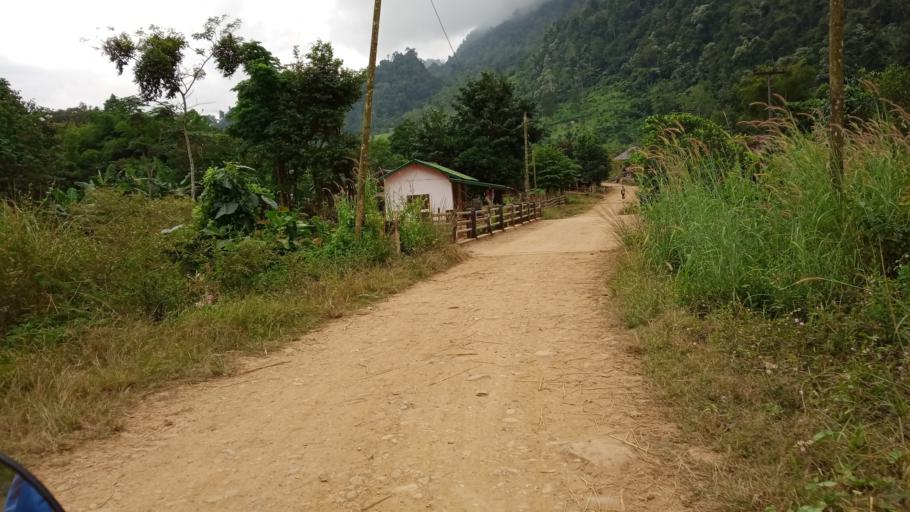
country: LA
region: Xiangkhoang
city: Phonsavan
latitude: 19.0842
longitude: 103.0122
